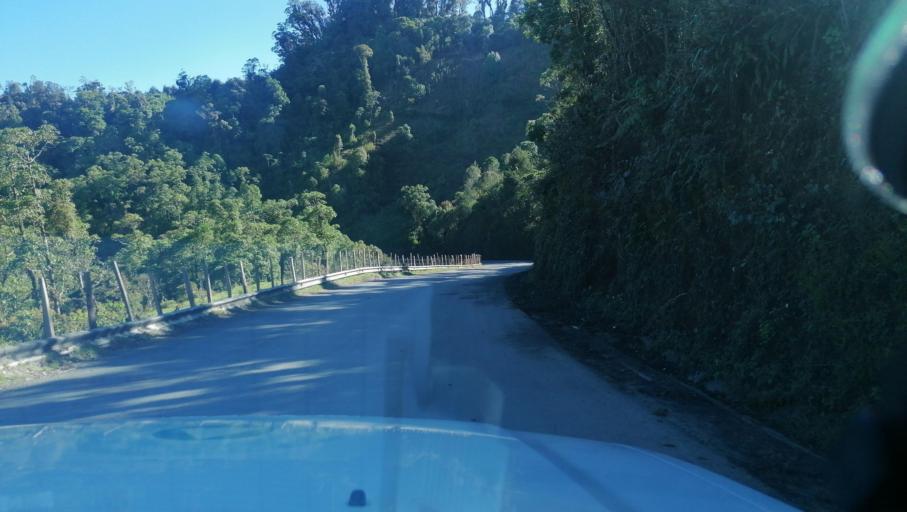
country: MX
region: Chiapas
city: Motozintla de Mendoza
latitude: 15.2709
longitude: -92.2303
